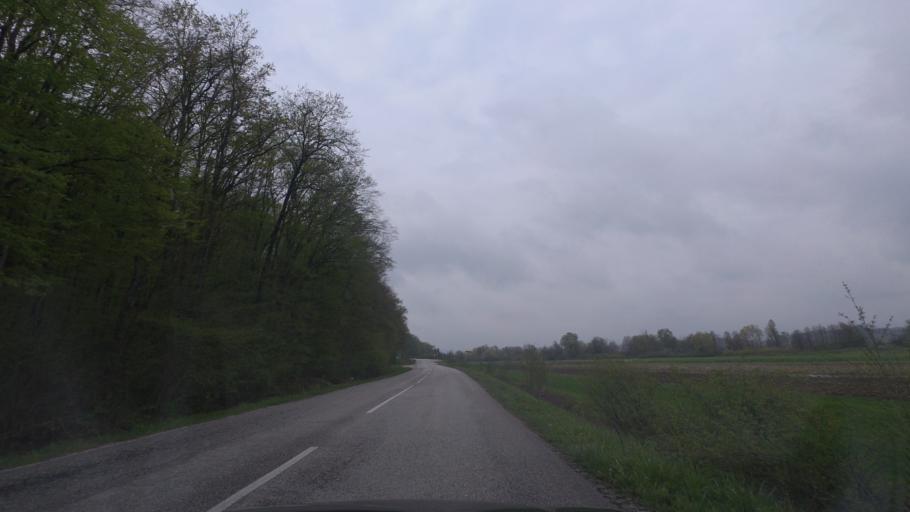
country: HR
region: Karlovacka
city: Ozalj
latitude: 45.6237
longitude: 15.5578
